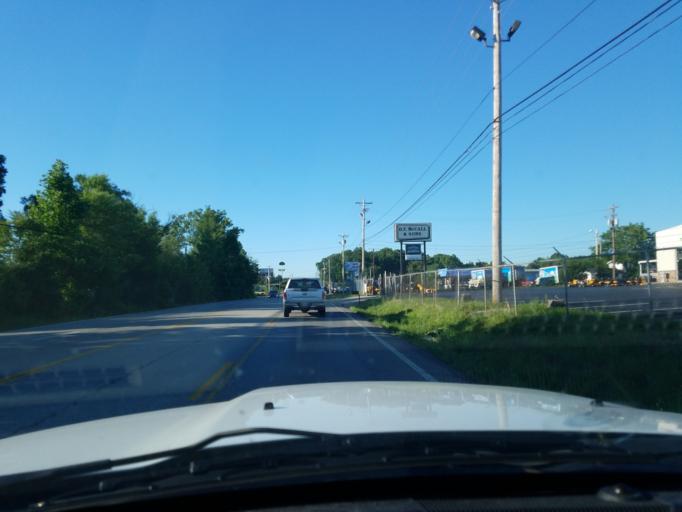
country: US
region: Tennessee
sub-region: Putnam County
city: Cookeville
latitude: 36.1274
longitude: -85.5060
